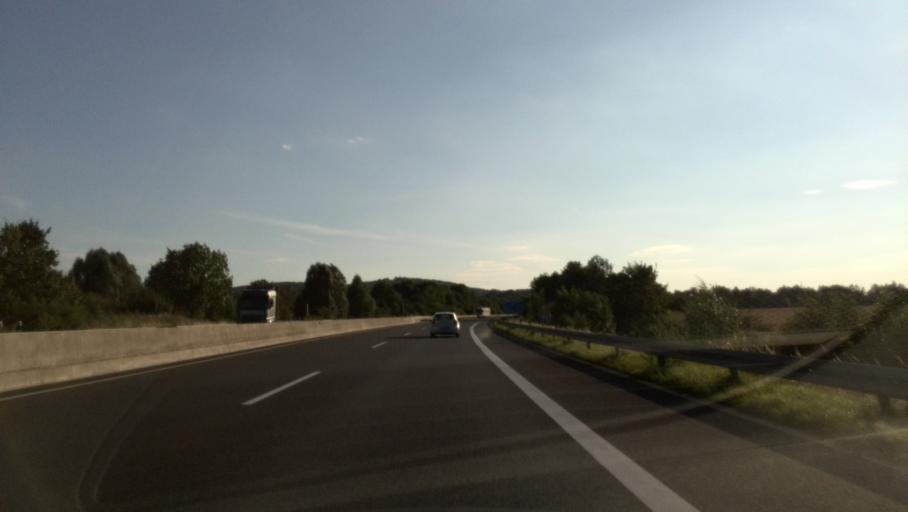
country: DE
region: Lower Saxony
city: Elbe
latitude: 52.1369
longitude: 10.3226
